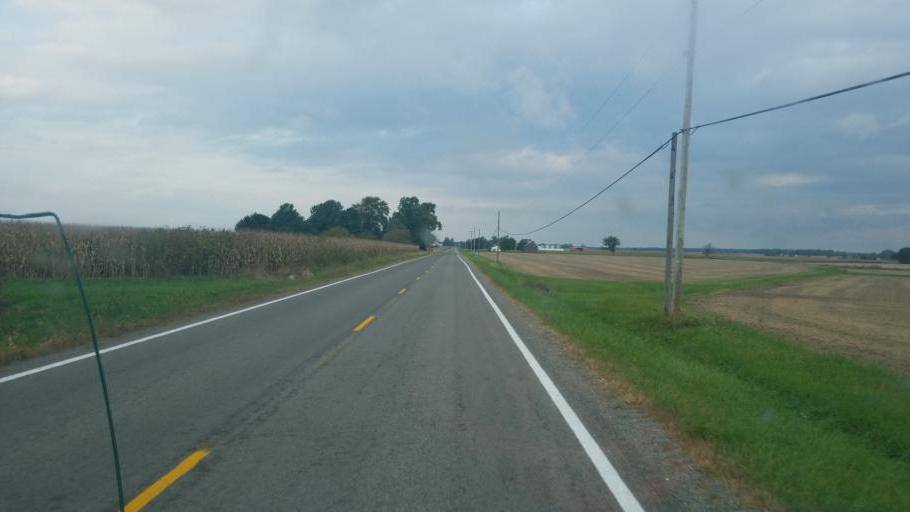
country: US
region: Ohio
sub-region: Marion County
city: Marion
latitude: 40.6878
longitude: -83.1708
